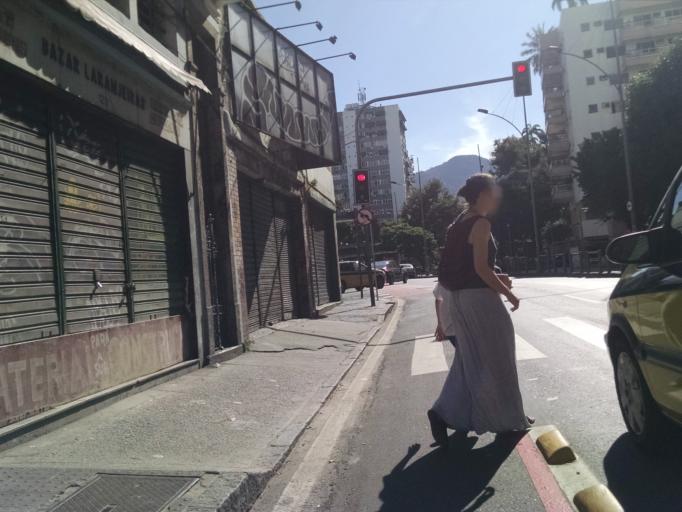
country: BR
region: Rio de Janeiro
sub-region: Rio De Janeiro
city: Rio de Janeiro
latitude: -22.9327
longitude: -43.1834
